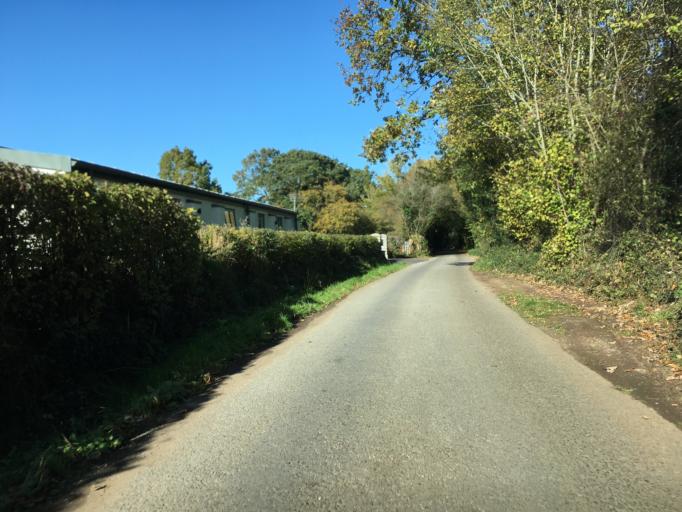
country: GB
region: England
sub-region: South Gloucestershire
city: Yate
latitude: 51.5526
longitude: -2.4279
